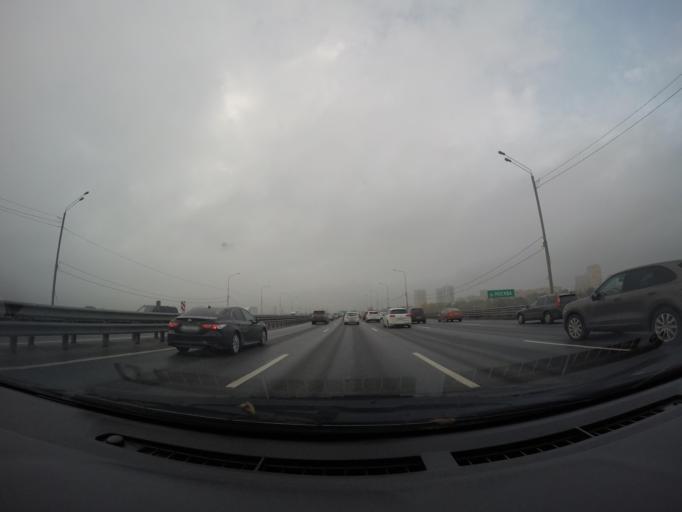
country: RU
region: Moskovskaya
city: Krasnogorsk
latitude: 55.8027
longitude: 37.3309
